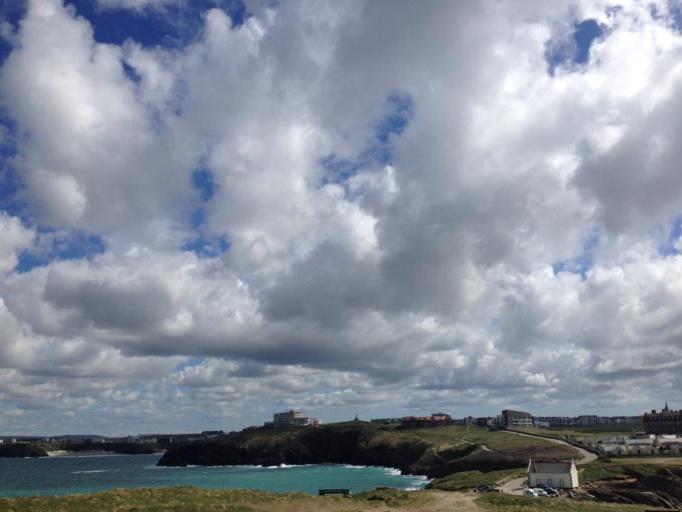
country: GB
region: England
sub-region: Cornwall
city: Newquay
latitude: 50.4250
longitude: -5.0991
